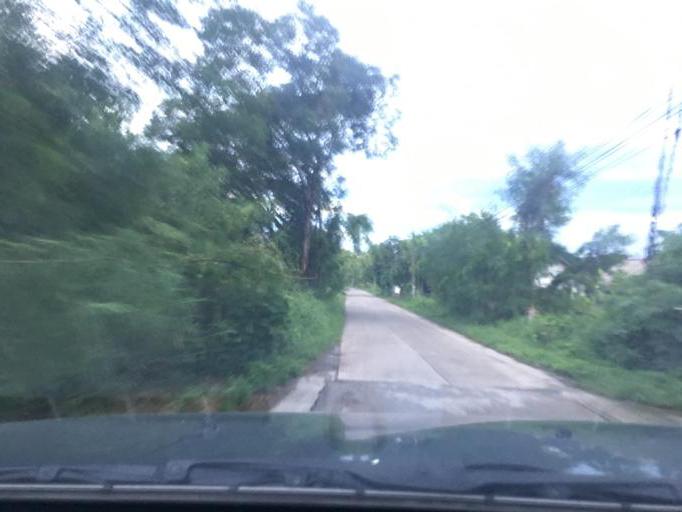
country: TH
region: Chiang Mai
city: San Sai
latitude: 18.8692
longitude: 98.9673
